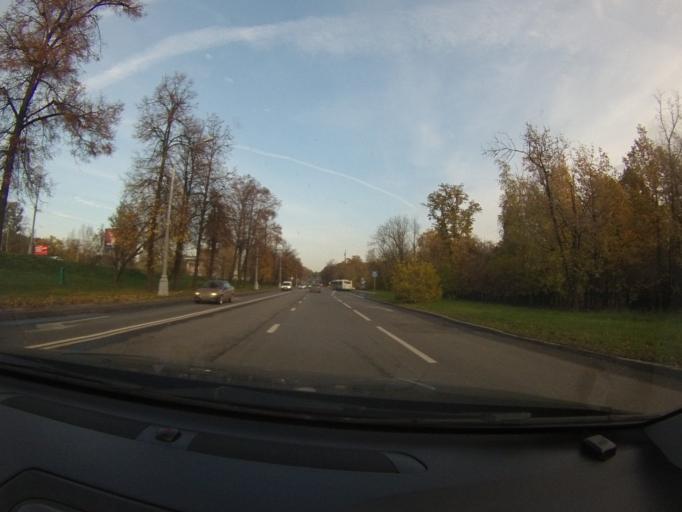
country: RU
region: Moscow
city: Davydkovo
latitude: 55.7289
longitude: 37.4796
